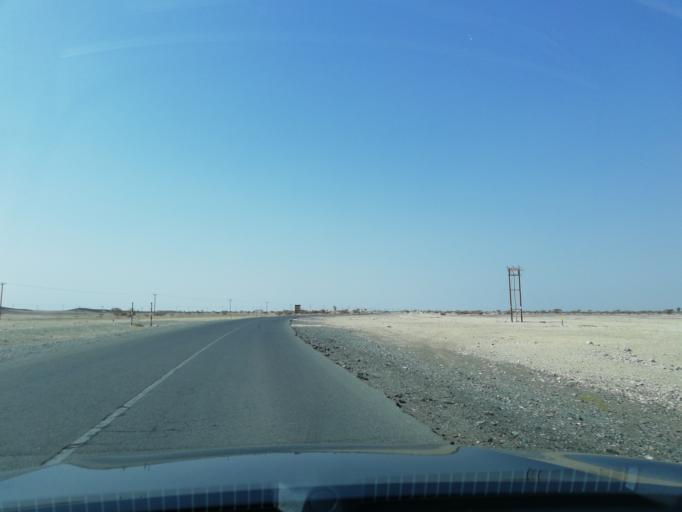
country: OM
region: Muhafazat ad Dakhiliyah
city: Adam
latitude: 22.3534
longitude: 58.0690
